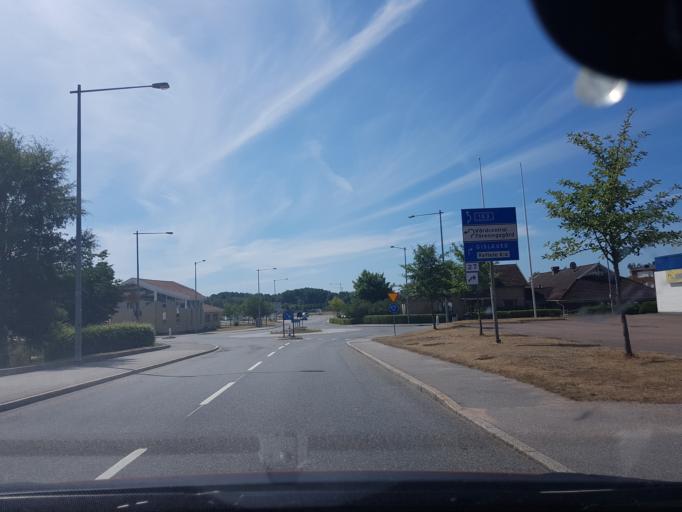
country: SE
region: Joenkoeping
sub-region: Gislaveds Kommun
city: Reftele
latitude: 57.1751
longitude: 13.5955
